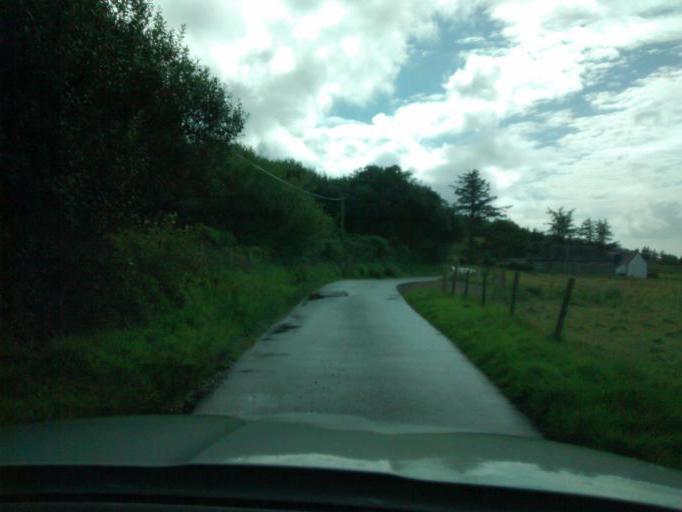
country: GB
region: Scotland
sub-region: North Ayrshire
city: Isle of Arran
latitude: 55.5754
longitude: -5.3455
